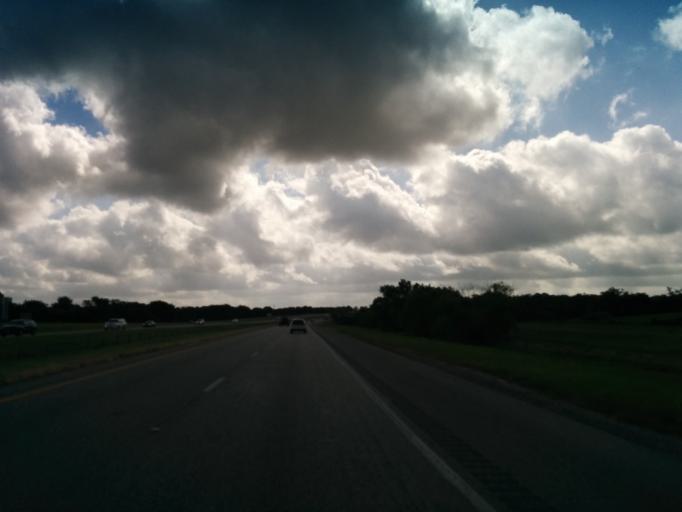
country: US
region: Texas
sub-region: Caldwell County
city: Luling
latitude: 29.6536
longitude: -97.5847
